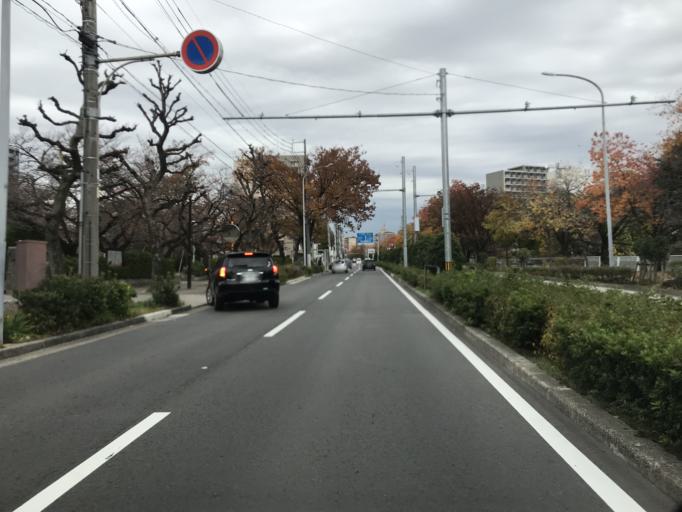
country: JP
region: Aichi
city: Nagoya-shi
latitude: 35.1868
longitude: 136.9001
